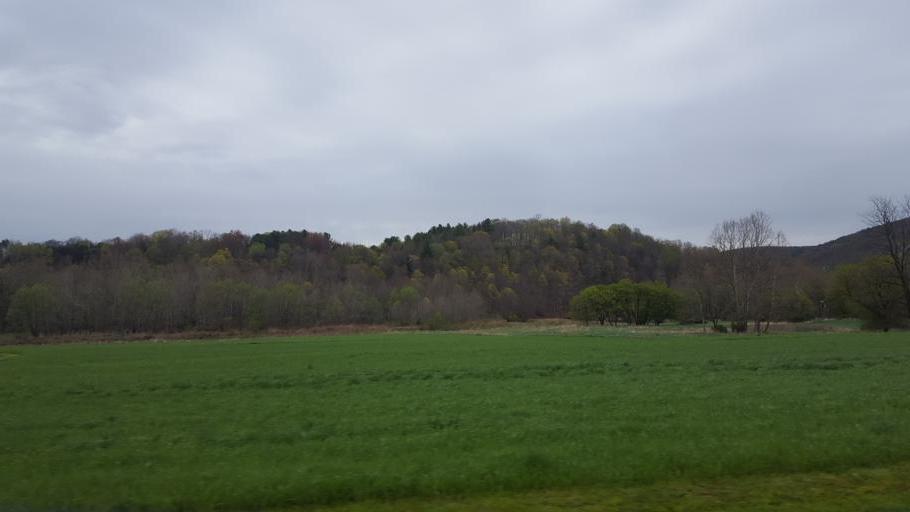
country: US
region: Pennsylvania
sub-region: Tioga County
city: Westfield
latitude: 41.9841
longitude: -77.4787
